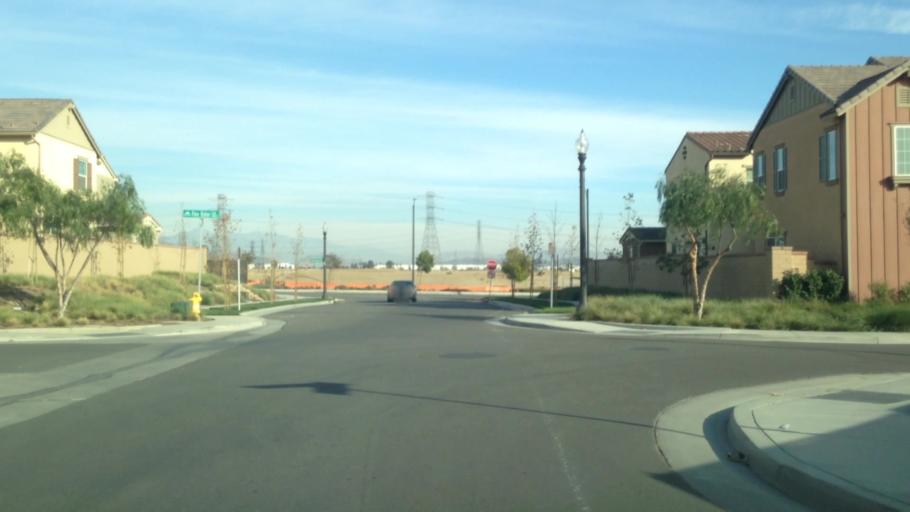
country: US
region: California
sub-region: Riverside County
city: Mira Loma
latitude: 34.0029
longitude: -117.5769
